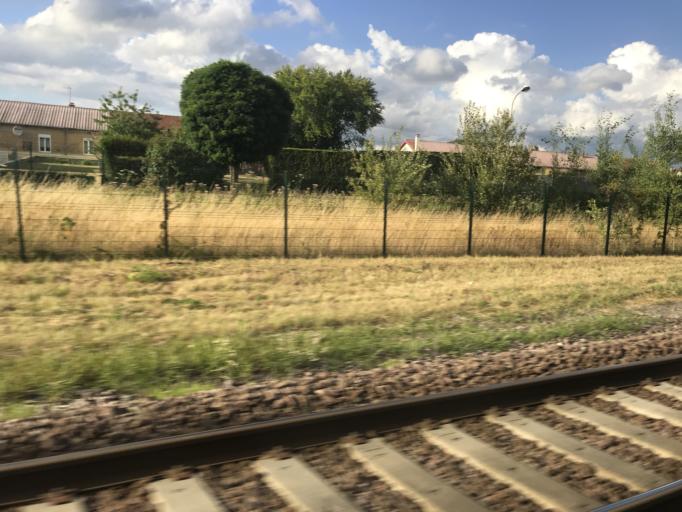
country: FR
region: Champagne-Ardenne
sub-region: Departement des Ardennes
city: Donchery
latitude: 49.6980
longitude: 4.8774
